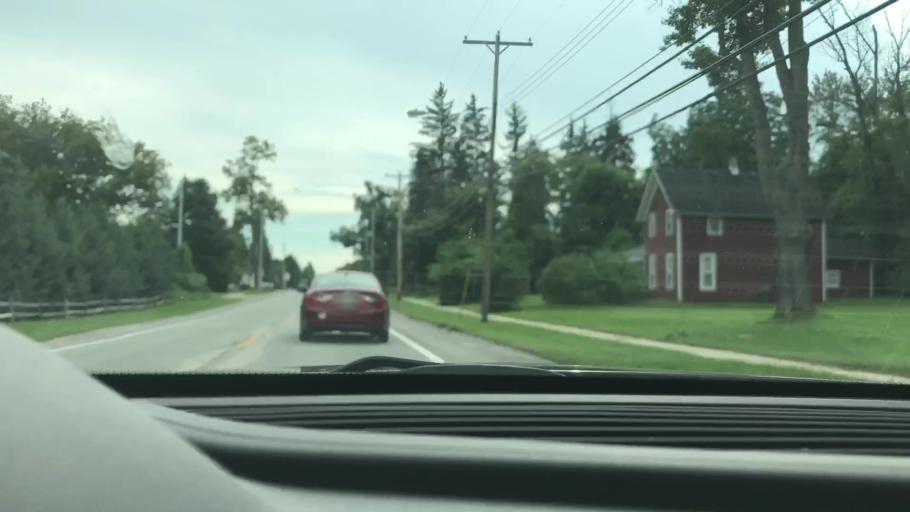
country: US
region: Michigan
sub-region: Antrim County
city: Bellaire
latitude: 45.0742
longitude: -85.2642
